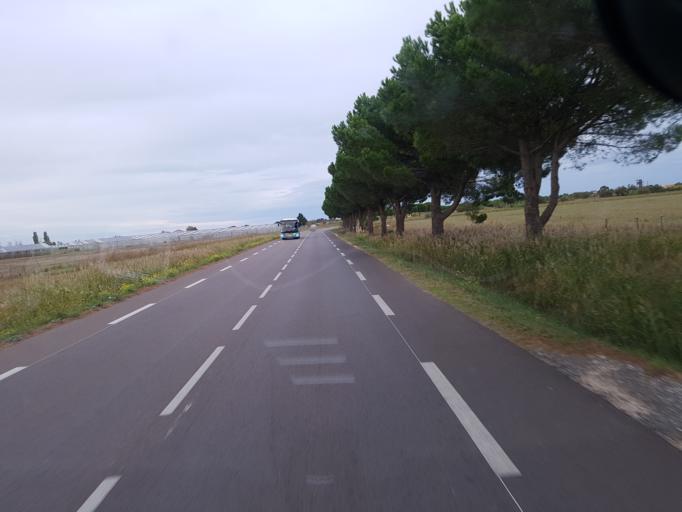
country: FR
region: Languedoc-Roussillon
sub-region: Departement des Pyrenees-Orientales
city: Torreilles
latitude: 42.7587
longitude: 3.0109
